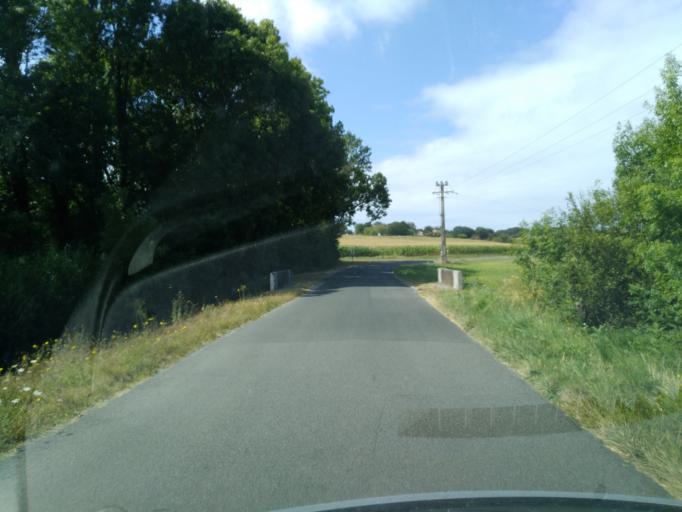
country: FR
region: Poitou-Charentes
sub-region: Departement de la Charente-Maritime
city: Breuillet
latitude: 45.6803
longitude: -1.0831
